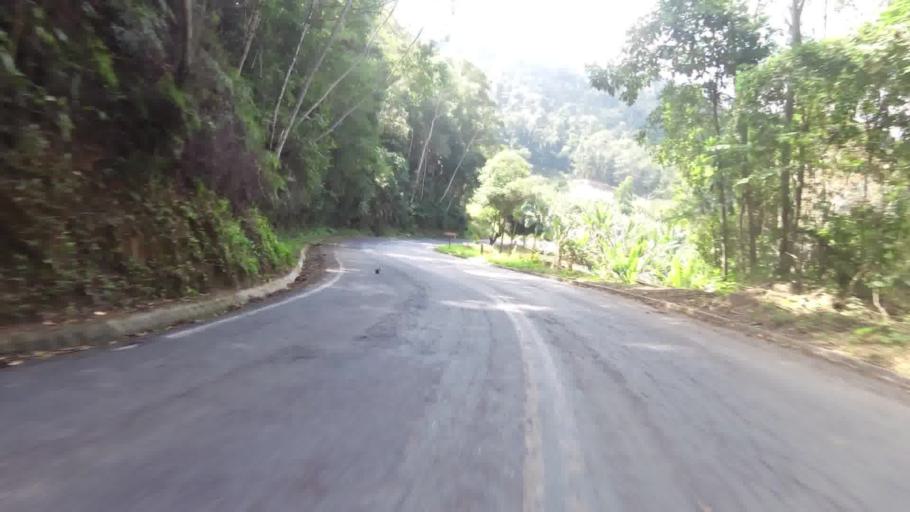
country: BR
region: Espirito Santo
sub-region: Alfredo Chaves
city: Alfredo Chaves
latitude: -20.5769
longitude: -40.8006
